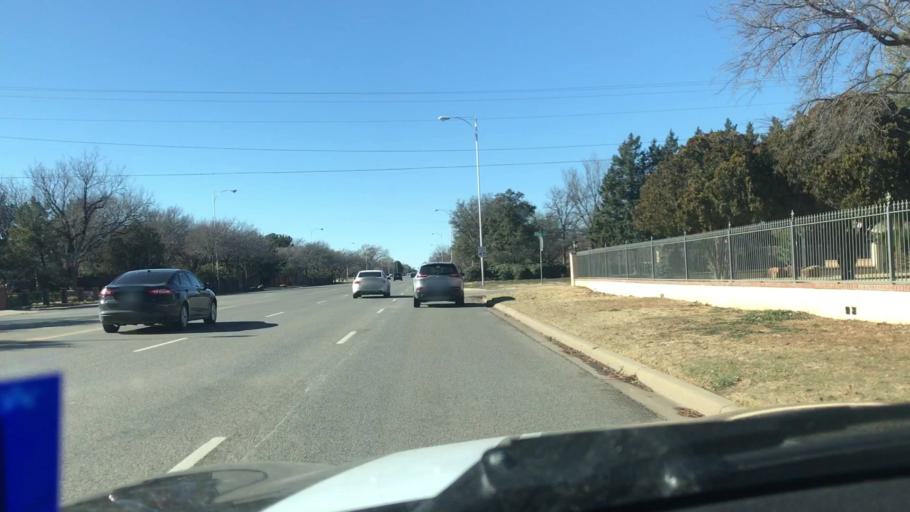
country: US
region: Texas
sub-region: Lubbock County
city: Lubbock
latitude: 33.5779
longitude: -101.9135
